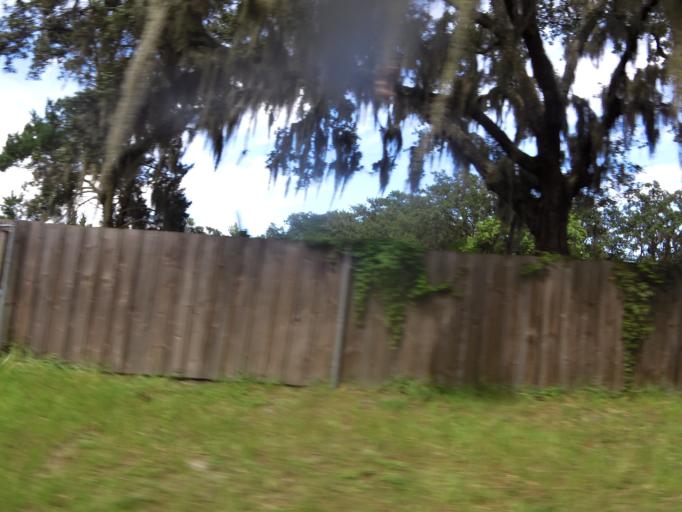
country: US
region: Florida
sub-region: Clay County
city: Lakeside
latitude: 30.1304
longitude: -81.7692
